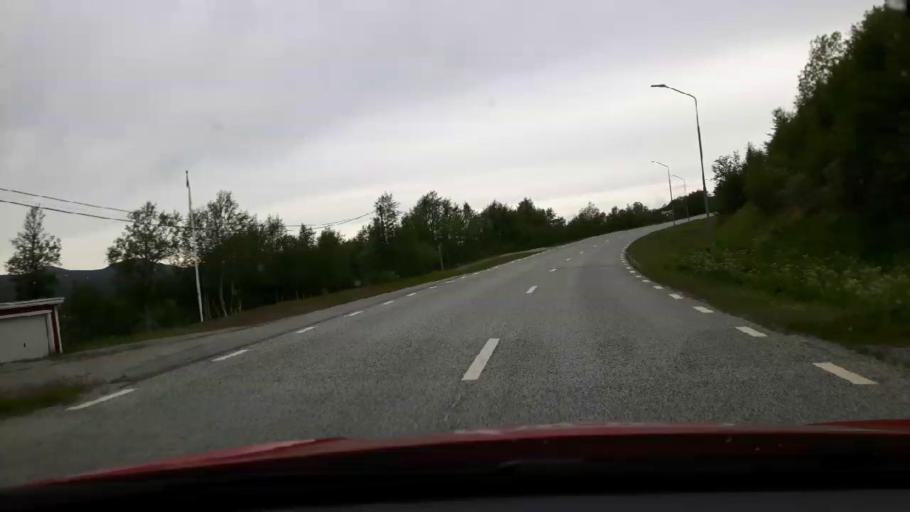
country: NO
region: Sor-Trondelag
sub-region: Tydal
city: Aas
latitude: 62.5942
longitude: 12.1849
